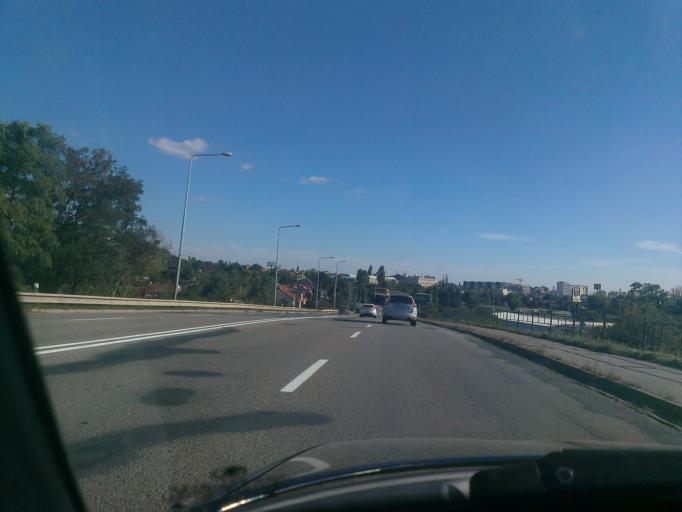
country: CZ
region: South Moravian
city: Podoli
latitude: 49.1884
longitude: 16.6644
